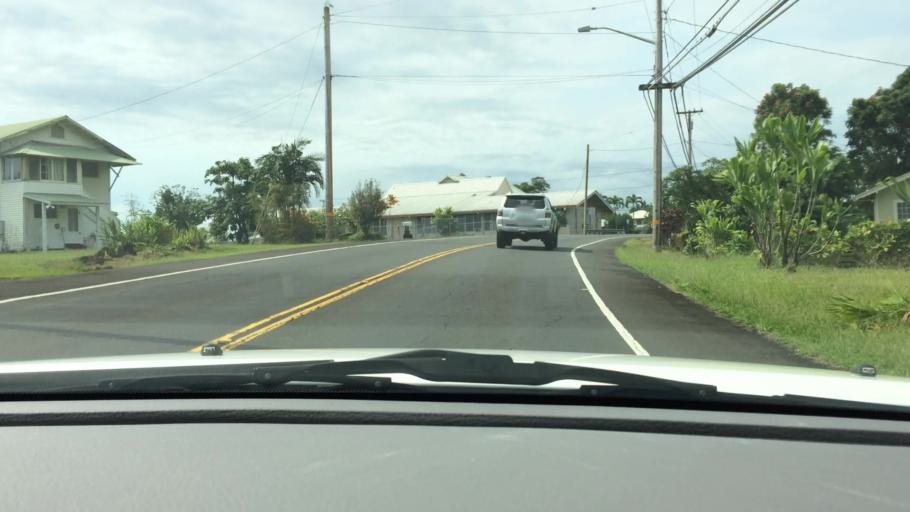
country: US
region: Hawaii
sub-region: Hawaii County
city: Hilo
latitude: 19.6960
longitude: -155.0702
